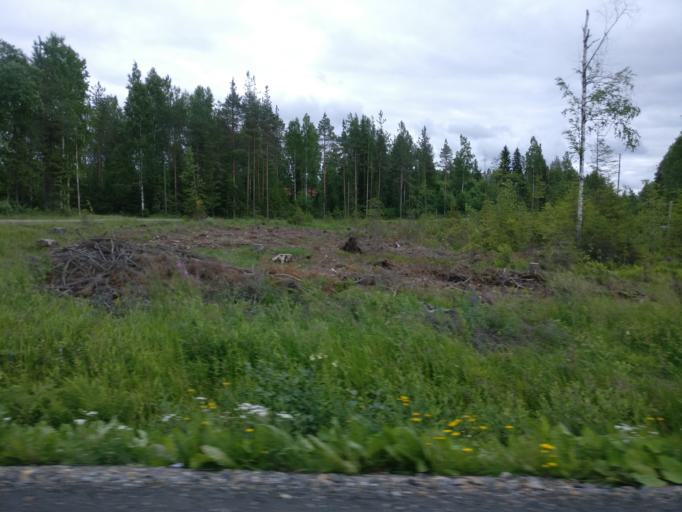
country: FI
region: Northern Savo
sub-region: Varkaus
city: Leppaevirta
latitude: 62.6192
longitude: 27.6223
